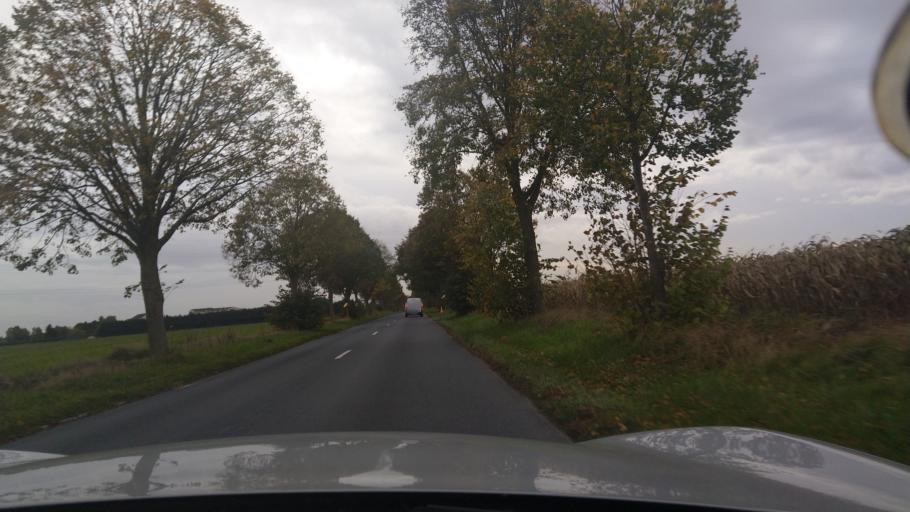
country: FR
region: Ile-de-France
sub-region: Departement de Seine-Saint-Denis
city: Villepinte
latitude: 48.9748
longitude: 2.5551
